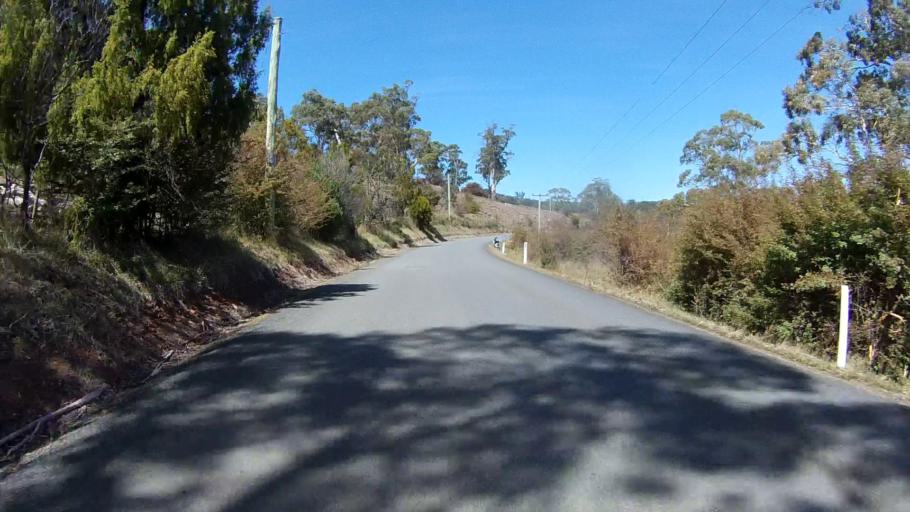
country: AU
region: Tasmania
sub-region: Sorell
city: Sorell
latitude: -42.7593
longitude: 147.6526
